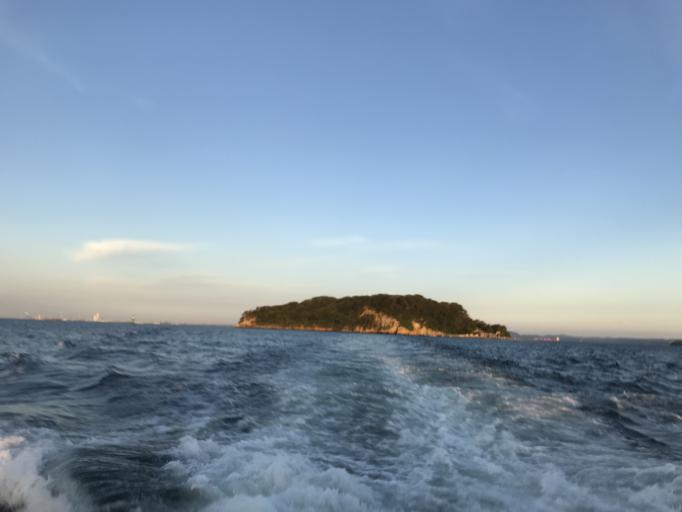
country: JP
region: Kanagawa
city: Yokosuka
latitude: 35.2861
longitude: 139.6851
